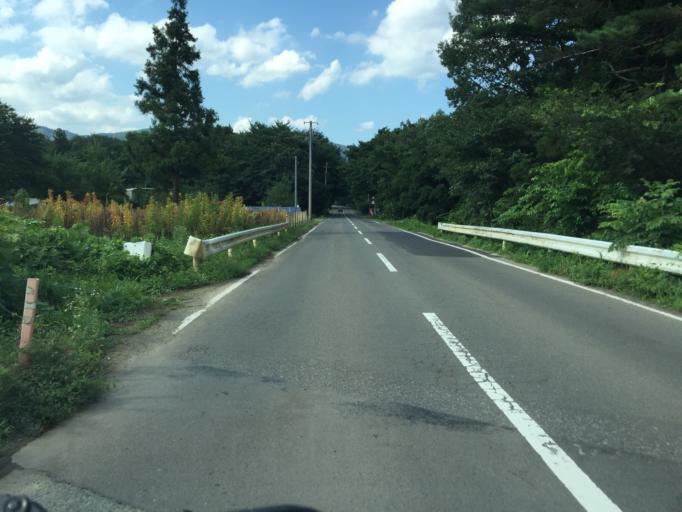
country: JP
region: Fukushima
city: Fukushima-shi
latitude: 37.7629
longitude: 140.3611
